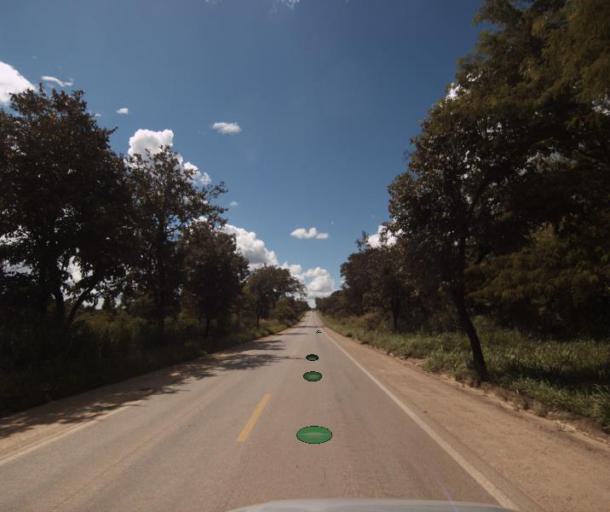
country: BR
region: Goias
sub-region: Porangatu
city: Porangatu
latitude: -13.6978
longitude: -49.0218
